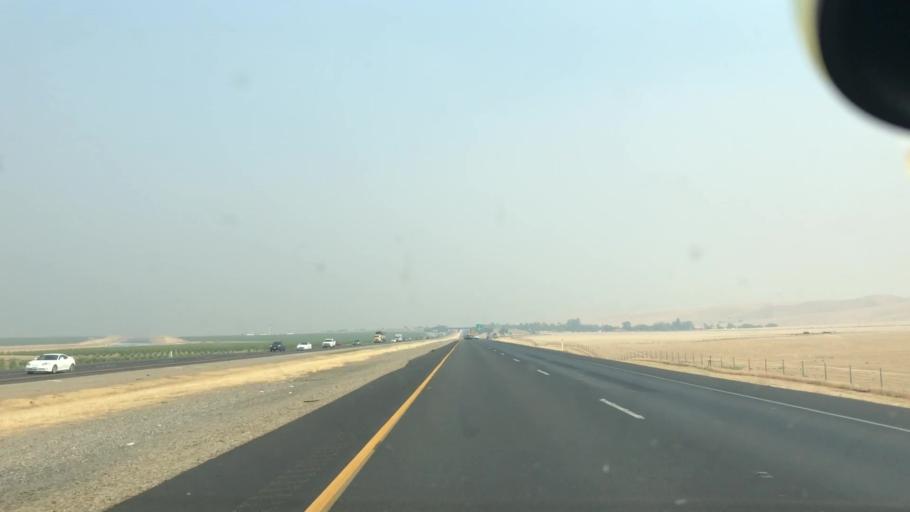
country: US
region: California
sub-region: San Joaquin County
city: Tracy
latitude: 37.6487
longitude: -121.4186
